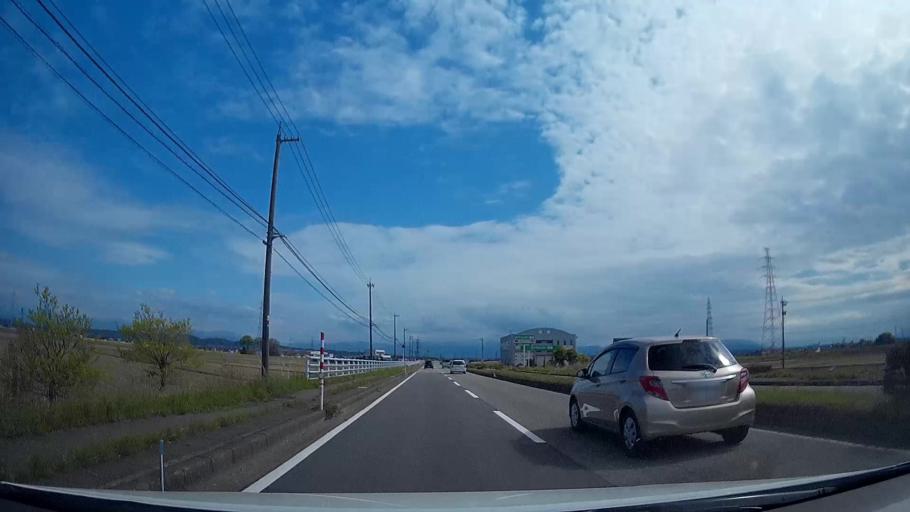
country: JP
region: Toyama
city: Kuragaki-kosugi
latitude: 36.7419
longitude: 137.1297
